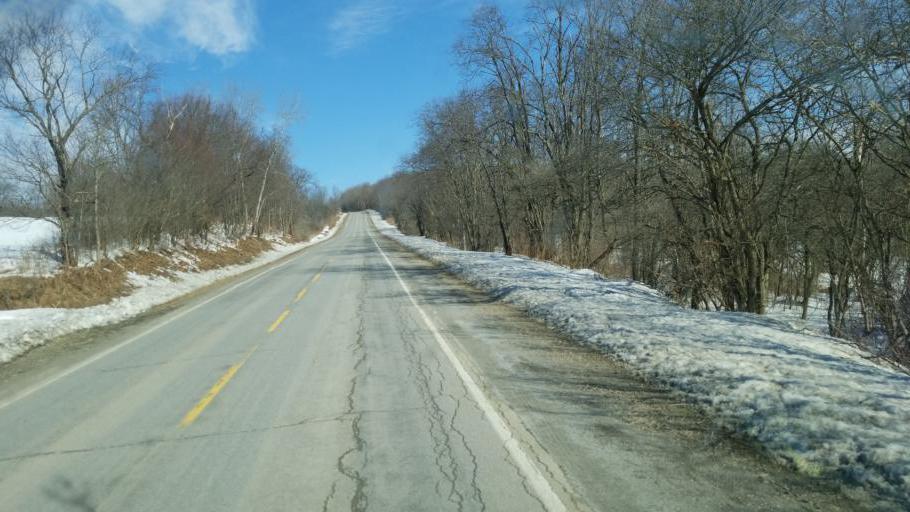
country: US
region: New York
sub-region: Allegany County
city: Andover
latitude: 42.1750
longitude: -77.7438
